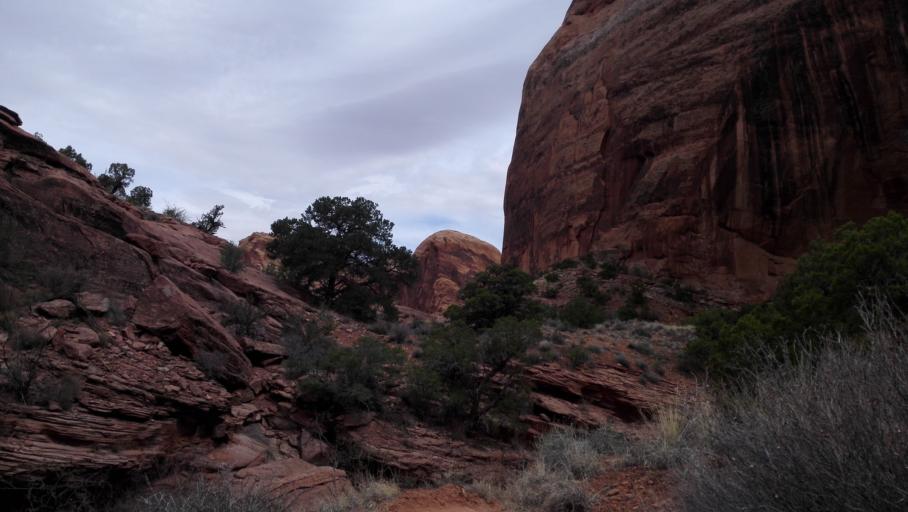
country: US
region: Utah
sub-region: Grand County
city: Moab
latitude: 38.4537
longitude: -109.9404
